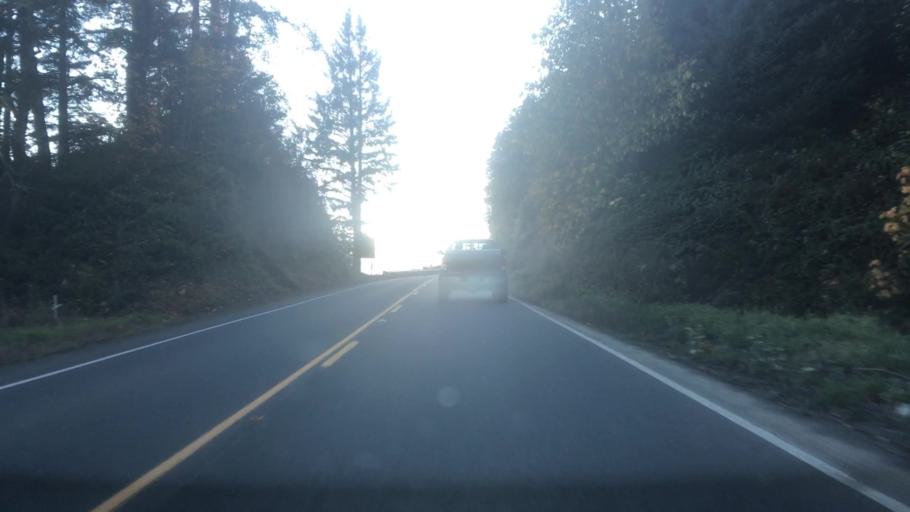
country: US
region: Oregon
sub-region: Clatsop County
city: Astoria
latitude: 46.2464
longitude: -123.8683
